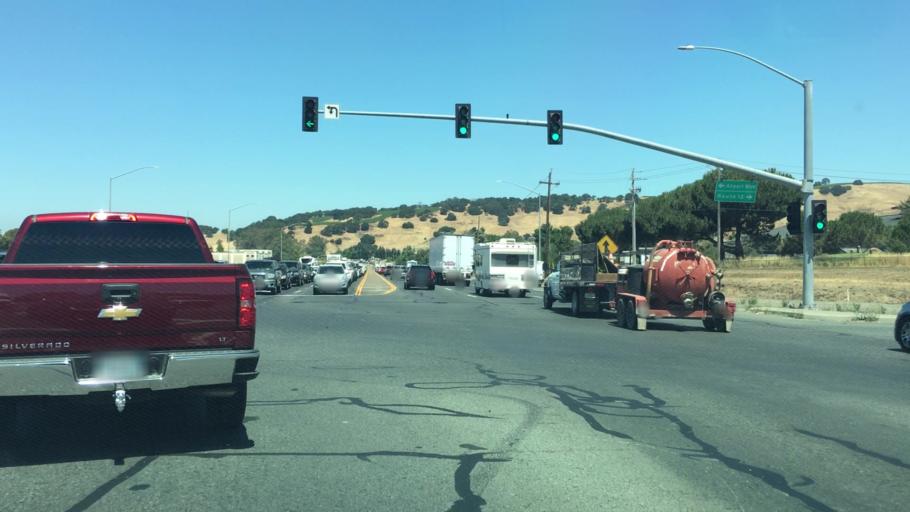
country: US
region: California
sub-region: Napa County
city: American Canyon
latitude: 38.2230
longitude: -122.2579
